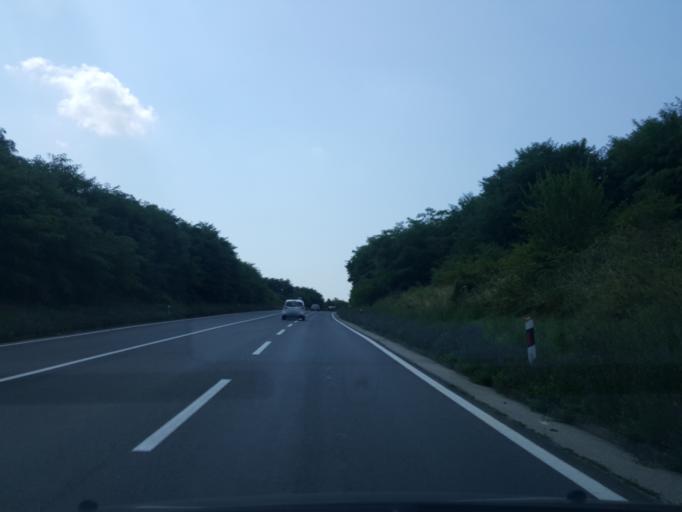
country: RS
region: Central Serbia
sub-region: Belgrade
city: Sopot
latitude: 44.5435
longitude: 20.6585
